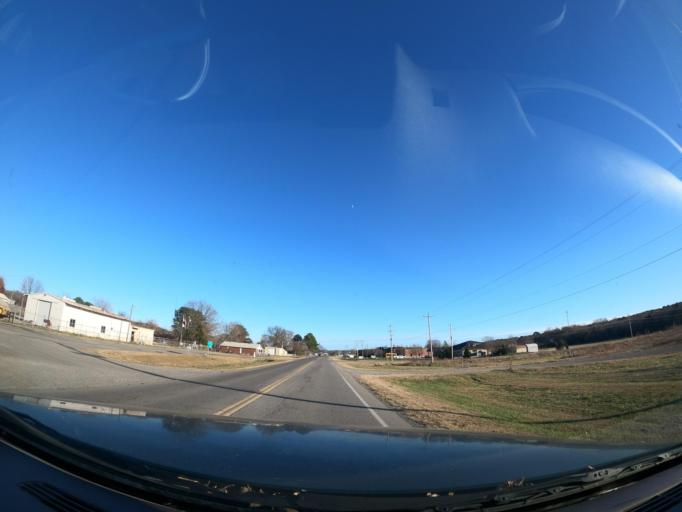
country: US
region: Oklahoma
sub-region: Latimer County
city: Wilburton
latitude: 34.9225
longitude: -95.3257
